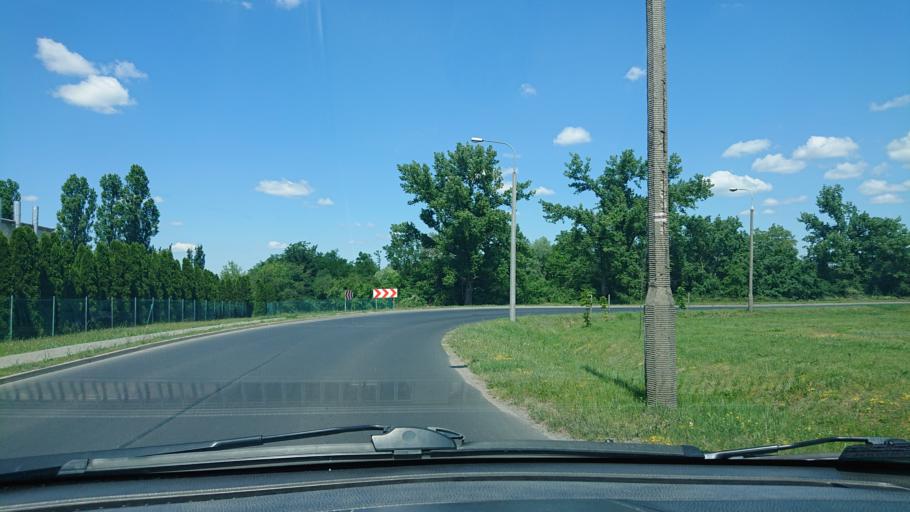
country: PL
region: Greater Poland Voivodeship
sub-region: Powiat gnieznienski
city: Gniezno
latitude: 52.5283
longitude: 17.6181
